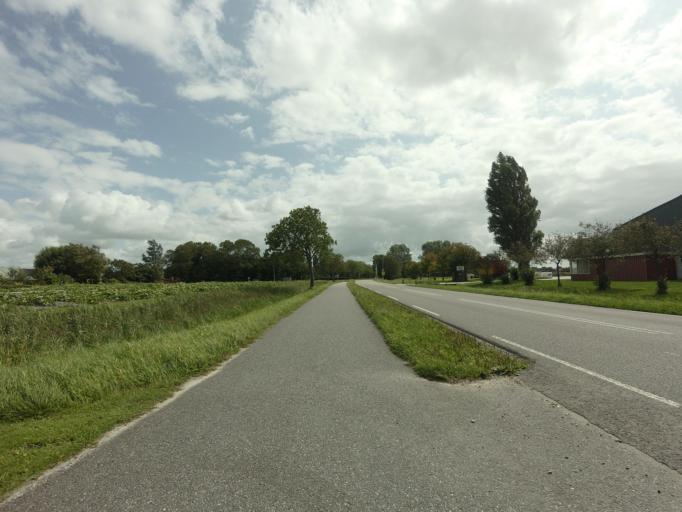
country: NL
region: Friesland
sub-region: Gemeente Harlingen
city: Harlingen
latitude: 53.1341
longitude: 5.4688
